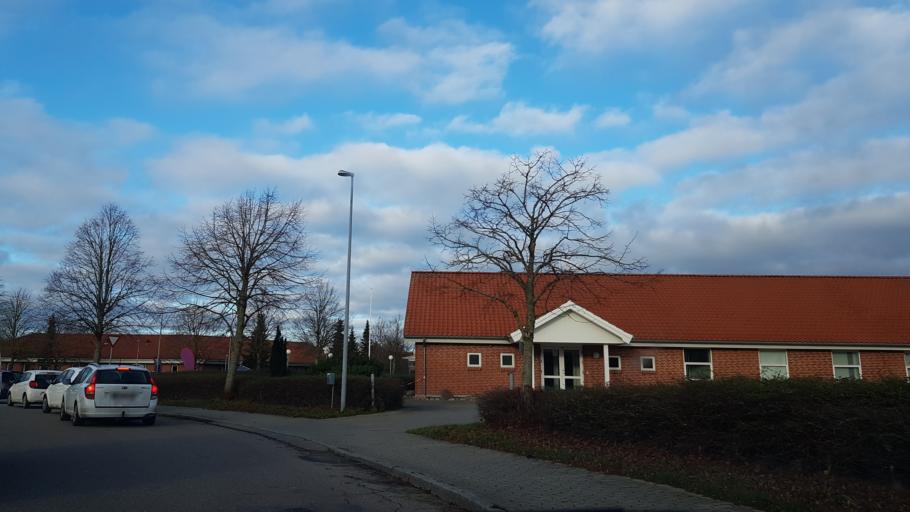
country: DK
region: Zealand
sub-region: Slagelse Kommune
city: Slagelse
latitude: 55.3885
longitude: 11.3299
